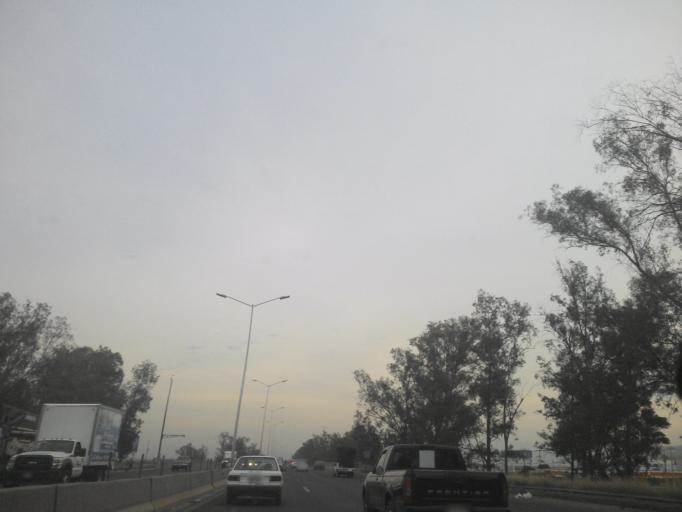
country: MX
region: Jalisco
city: Guadalajara
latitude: 20.6598
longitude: -103.4482
